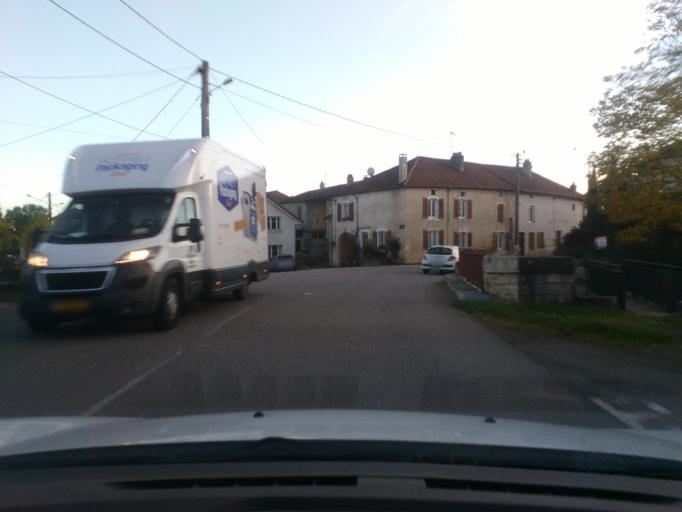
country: FR
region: Lorraine
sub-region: Departement des Vosges
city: Mirecourt
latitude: 48.3955
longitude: 6.1331
